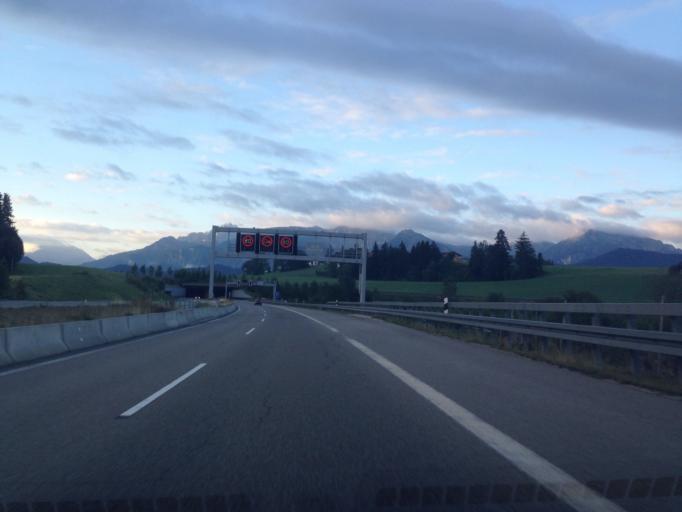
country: DE
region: Bavaria
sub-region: Swabia
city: Hopferau
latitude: 47.6074
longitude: 10.6555
